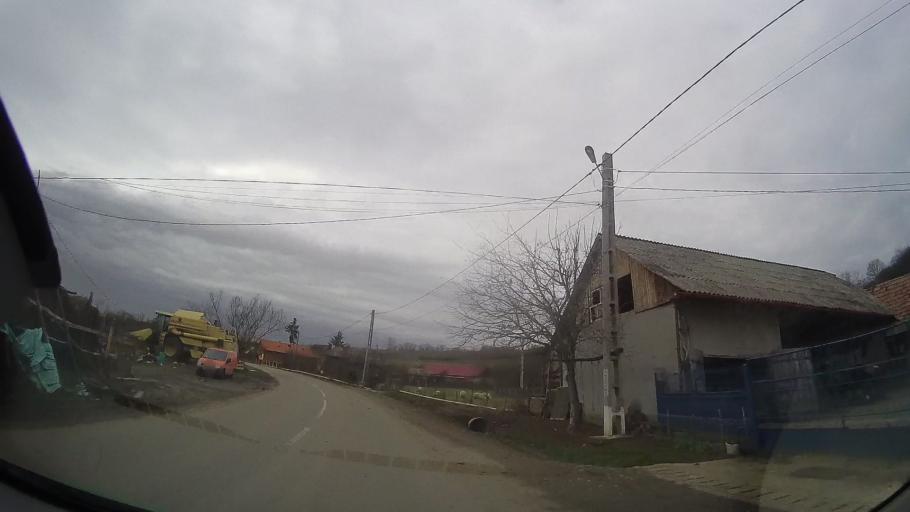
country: RO
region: Bistrita-Nasaud
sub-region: Comuna Milas
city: Milas
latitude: 46.8095
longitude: 24.4284
